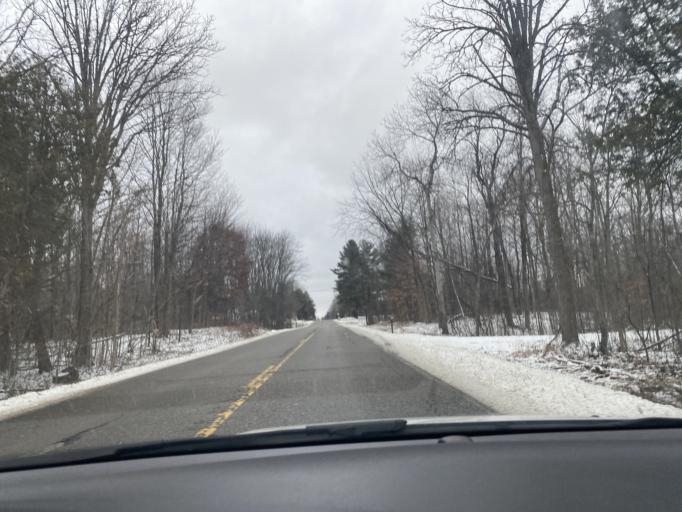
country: US
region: Michigan
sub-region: Lapeer County
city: Barnes Lake-Millers Lake
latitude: 43.2050
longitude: -83.2950
